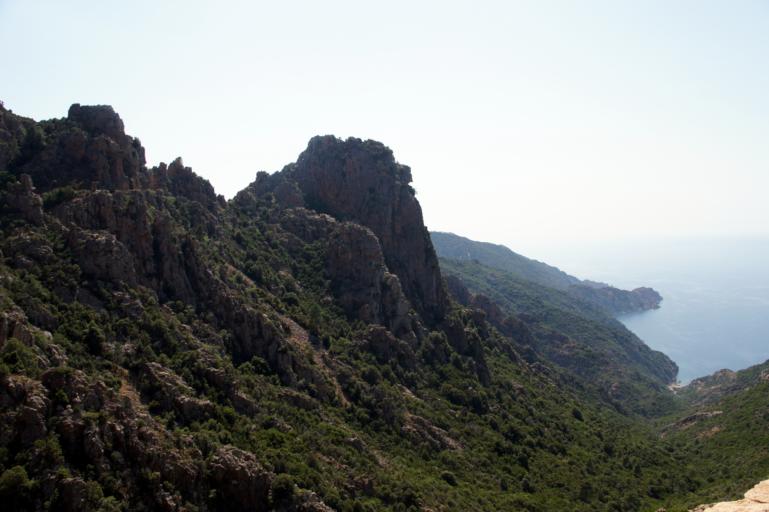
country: FR
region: Corsica
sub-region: Departement de la Corse-du-Sud
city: Cargese
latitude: 42.2494
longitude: 8.6602
